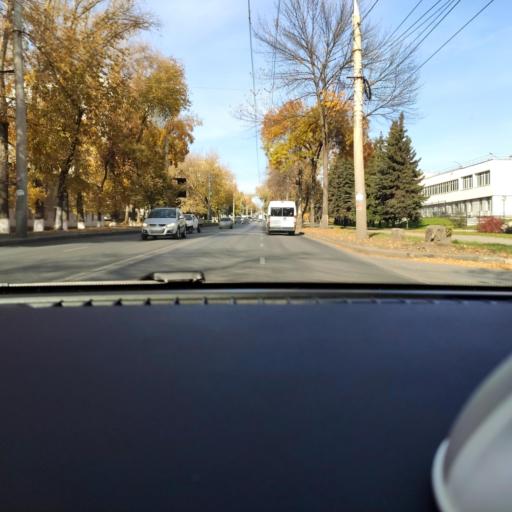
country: RU
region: Samara
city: Samara
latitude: 53.2379
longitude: 50.2393
